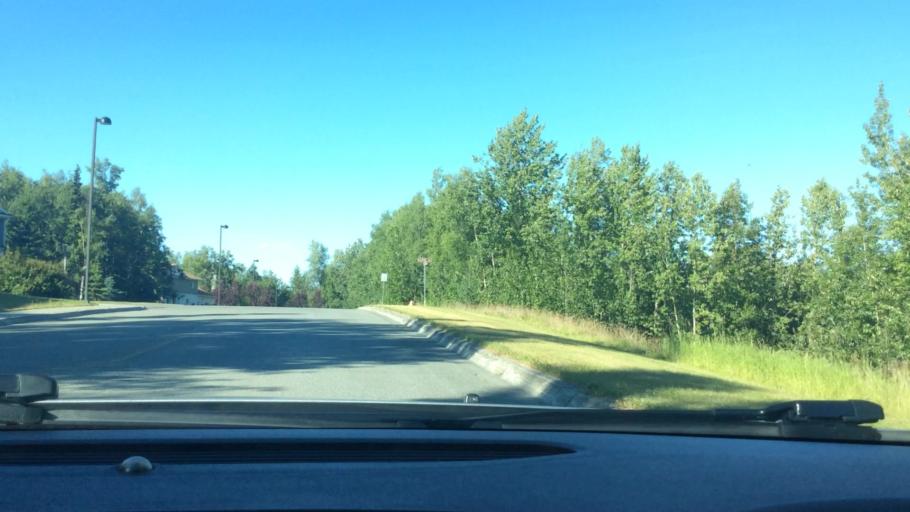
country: US
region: Alaska
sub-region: Anchorage Municipality
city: Elmendorf Air Force Base
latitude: 61.2499
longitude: -149.7016
